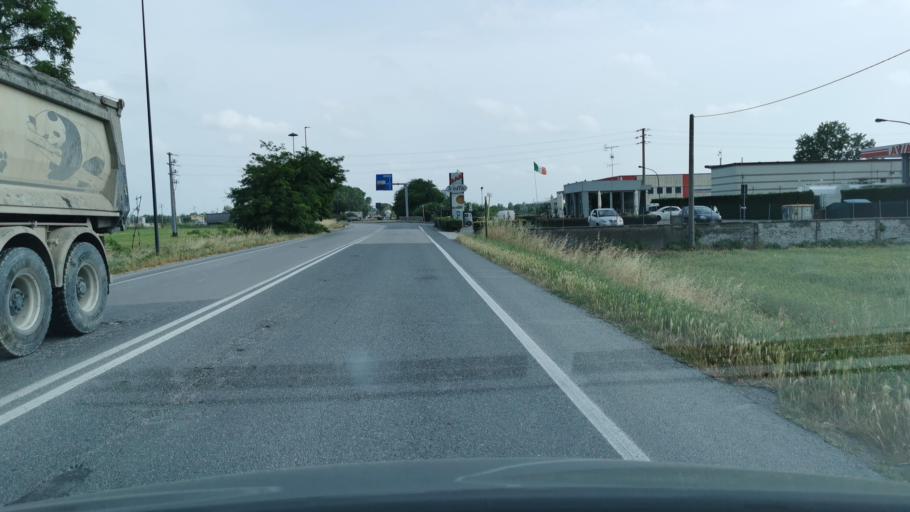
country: IT
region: Emilia-Romagna
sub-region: Provincia di Ravenna
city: Ravenna
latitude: 44.4448
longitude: 12.2105
